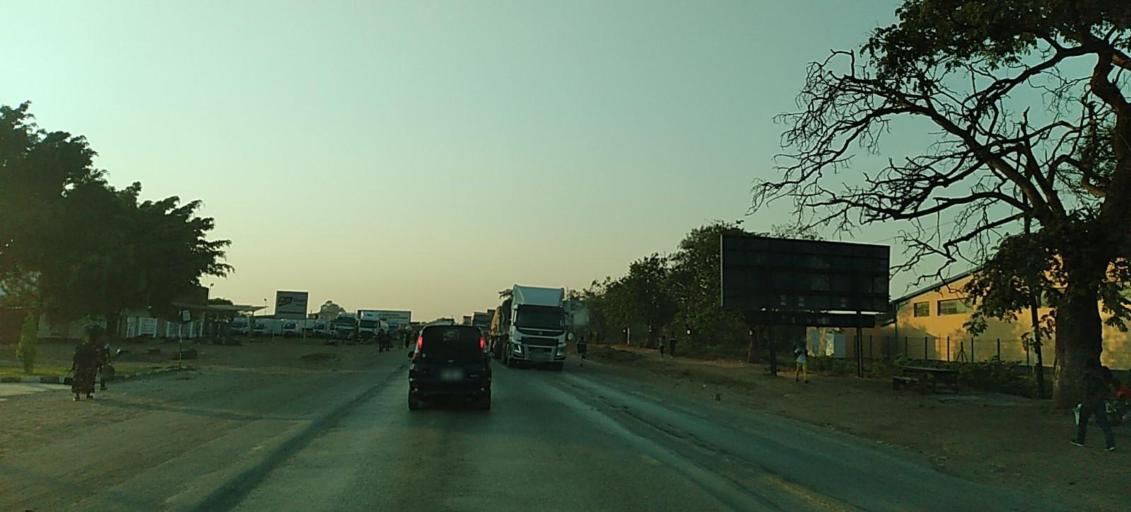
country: ZM
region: Copperbelt
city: Ndola
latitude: -13.0063
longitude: 28.6518
